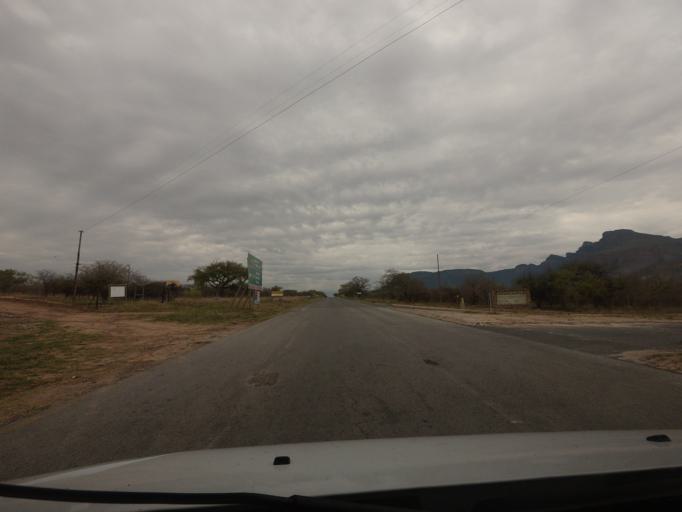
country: ZA
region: Limpopo
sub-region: Mopani District Municipality
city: Hoedspruit
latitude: -24.4779
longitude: 30.8836
